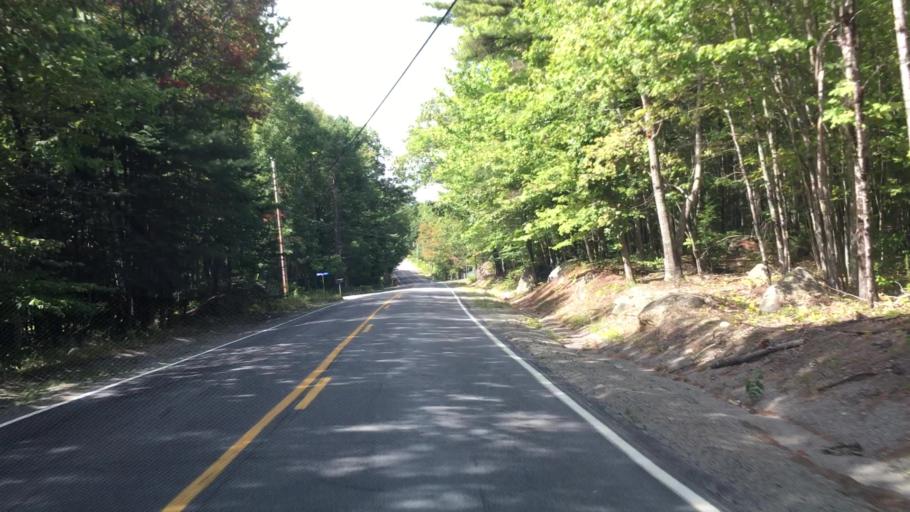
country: US
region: Maine
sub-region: Penobscot County
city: Holden
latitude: 44.7939
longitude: -68.5174
